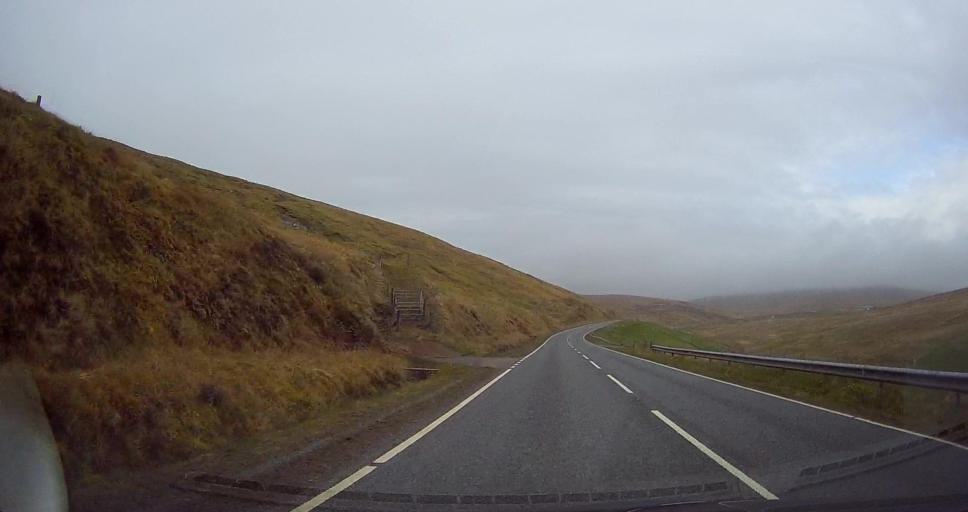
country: GB
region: Scotland
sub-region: Shetland Islands
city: Sandwick
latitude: 59.9960
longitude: -1.2787
